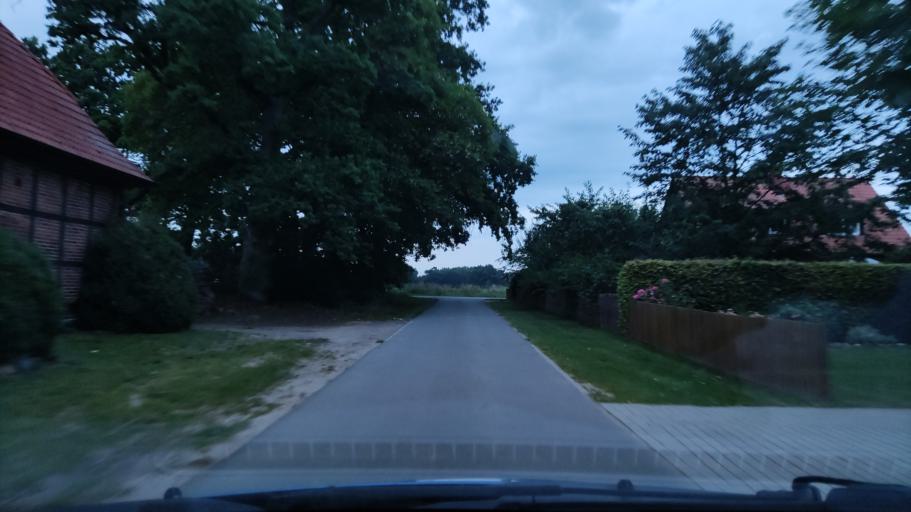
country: DE
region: Lower Saxony
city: Romstedt
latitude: 53.1638
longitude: 10.6678
